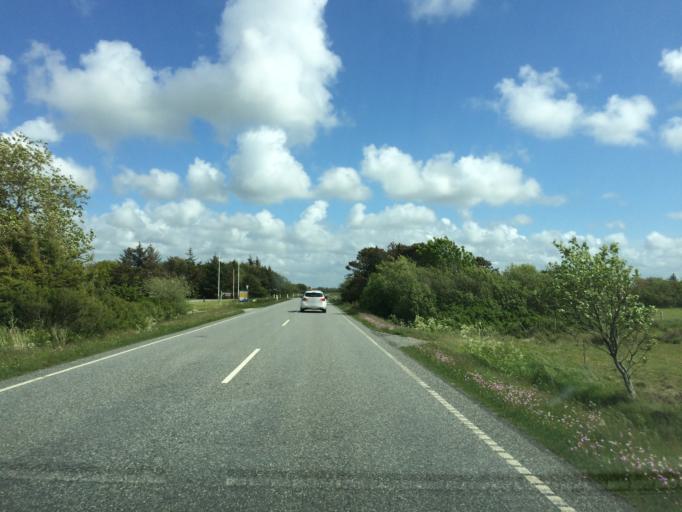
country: DK
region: Central Jutland
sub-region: Holstebro Kommune
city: Ulfborg
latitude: 56.3150
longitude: 8.1667
